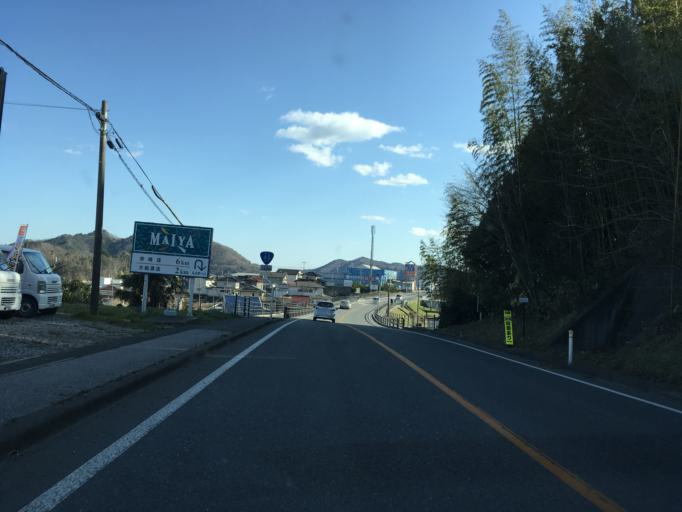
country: JP
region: Iwate
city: Ofunato
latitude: 39.0446
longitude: 141.7218
